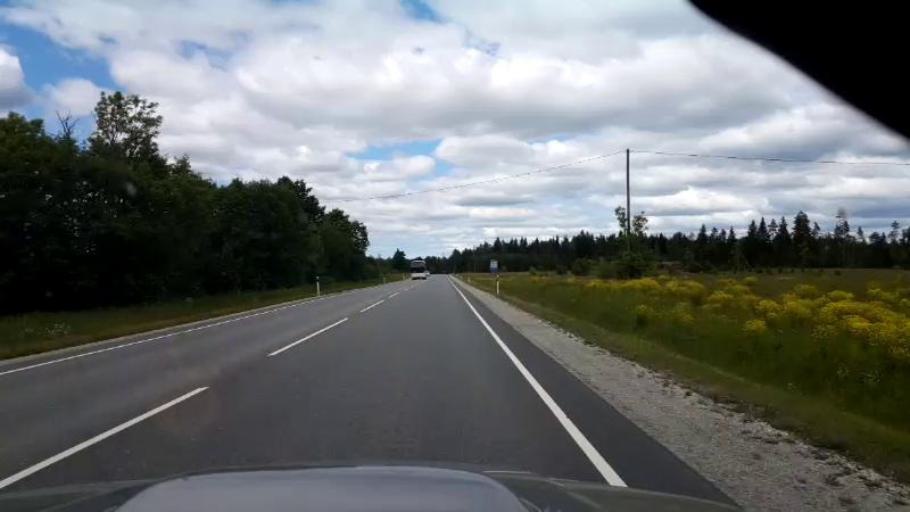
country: EE
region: Raplamaa
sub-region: Maerjamaa vald
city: Marjamaa
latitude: 58.9728
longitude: 24.4757
